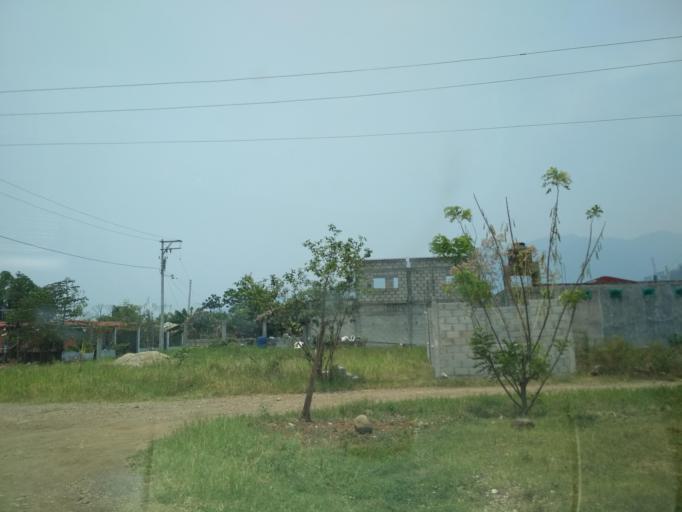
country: MX
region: Veracruz
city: Cosolapa
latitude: 18.5896
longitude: -96.6973
